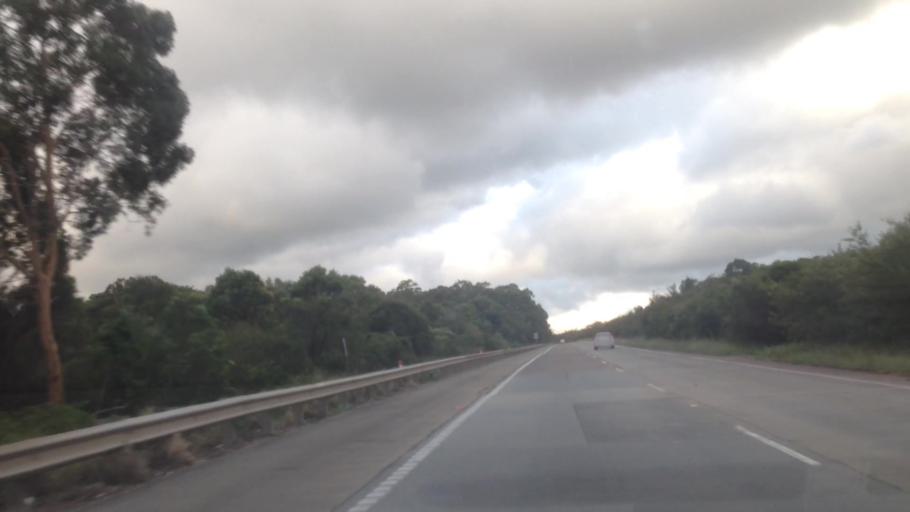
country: AU
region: New South Wales
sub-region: Wyong Shire
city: Jilliby
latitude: -33.2066
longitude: 151.4561
